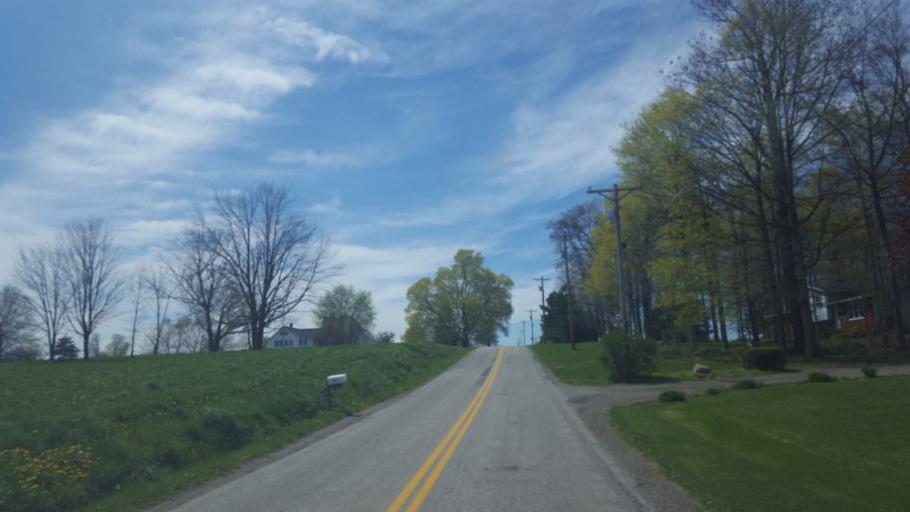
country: US
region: Ohio
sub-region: Ashland County
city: Ashland
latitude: 40.8060
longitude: -82.3262
